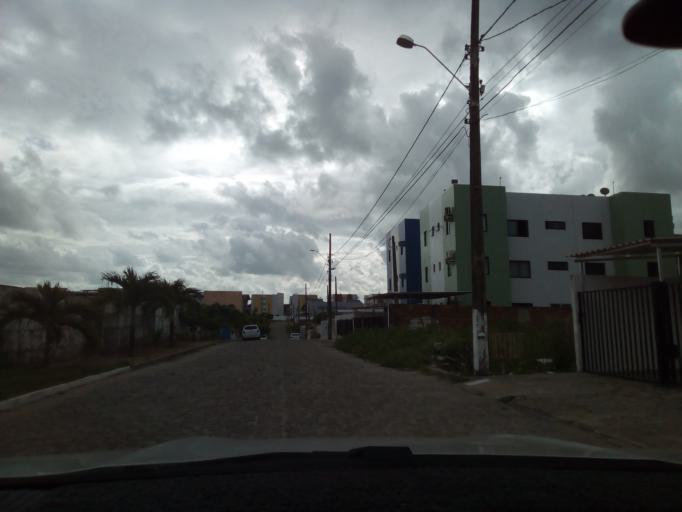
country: BR
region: Paraiba
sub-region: Joao Pessoa
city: Joao Pessoa
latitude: -7.1872
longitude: -34.8741
